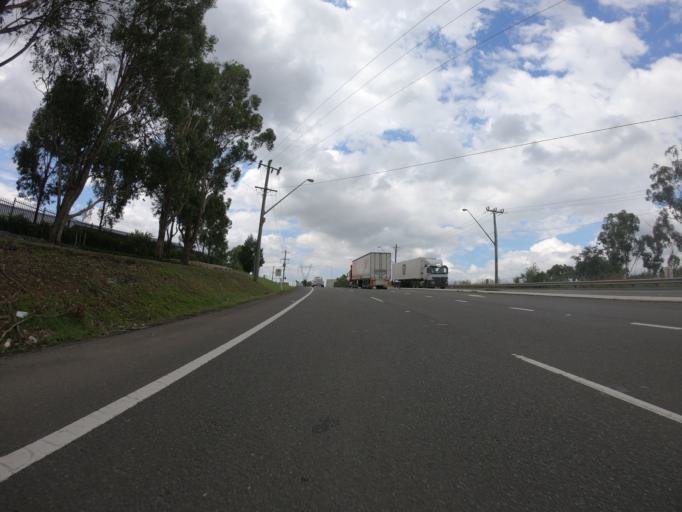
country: AU
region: New South Wales
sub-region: Blacktown
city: Mount Druitt
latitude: -33.8138
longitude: 150.7845
